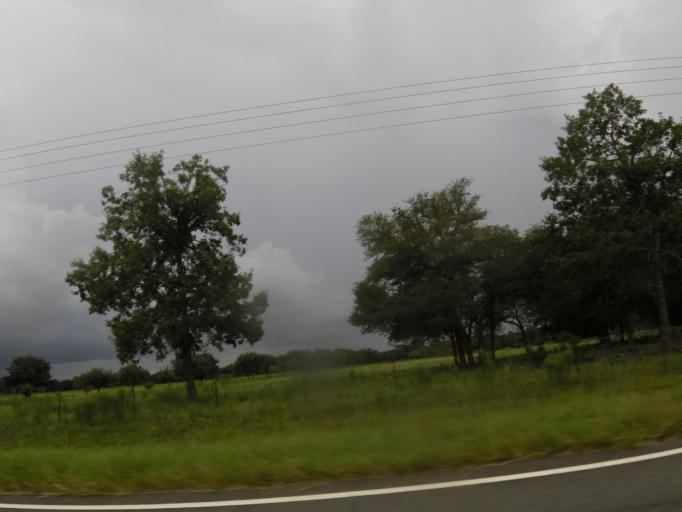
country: US
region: Florida
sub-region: Baker County
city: Macclenny
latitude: 30.4104
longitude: -82.1918
